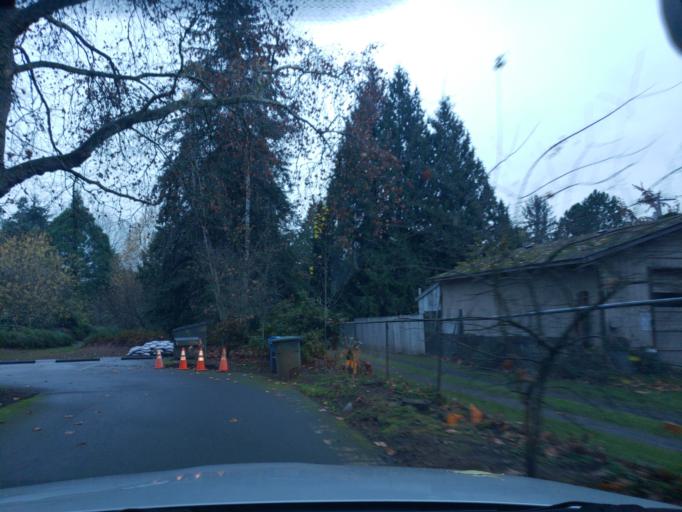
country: US
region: Washington
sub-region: King County
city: Kenmore
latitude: 47.7522
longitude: -122.2474
